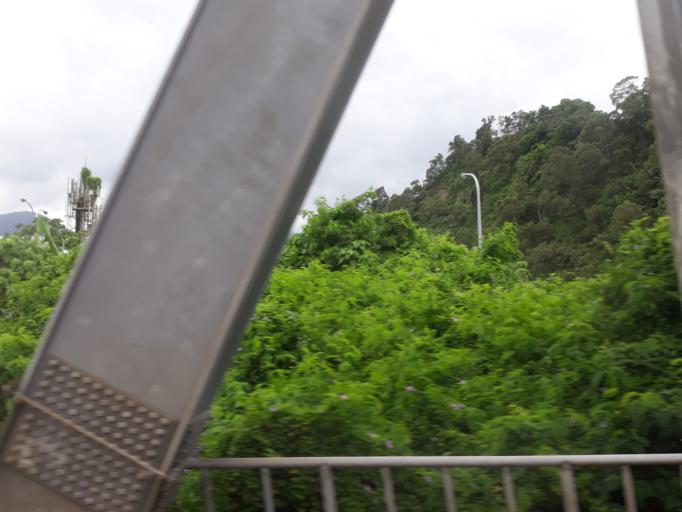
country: TW
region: Taiwan
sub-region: Yilan
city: Yilan
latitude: 24.6157
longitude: 121.8126
